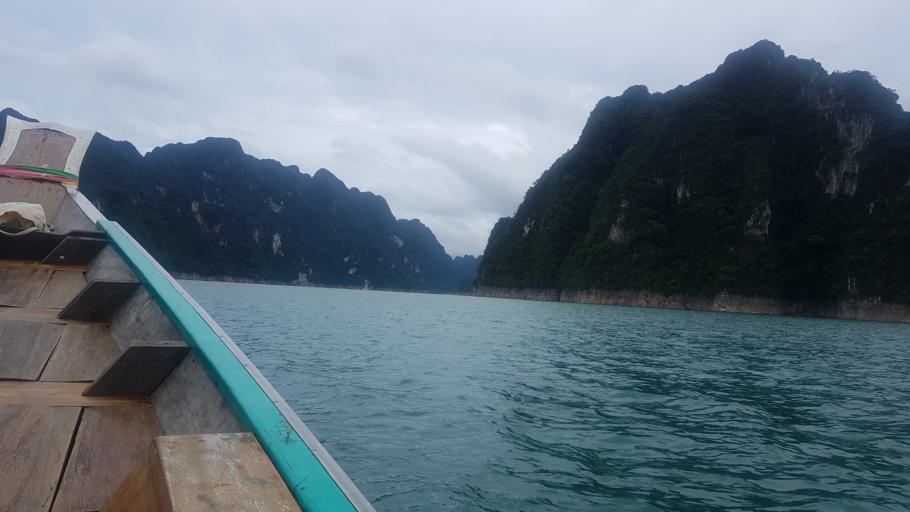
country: TH
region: Surat Thani
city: Phanom
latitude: 9.0248
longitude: 98.7226
